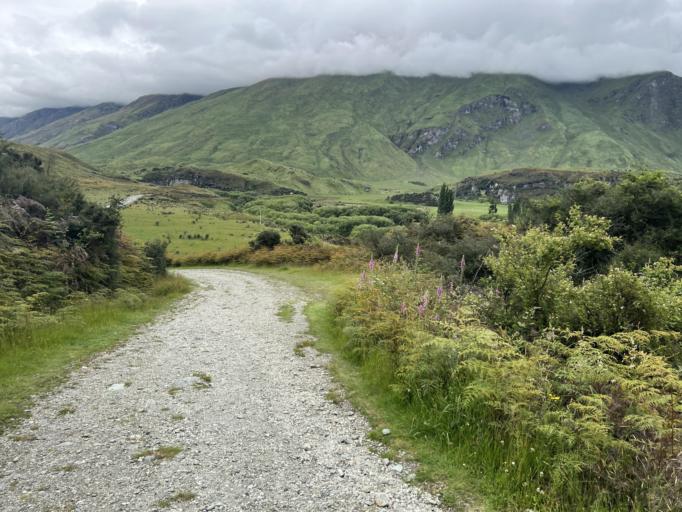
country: NZ
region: Otago
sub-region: Queenstown-Lakes District
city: Wanaka
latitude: -44.6493
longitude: 168.9599
